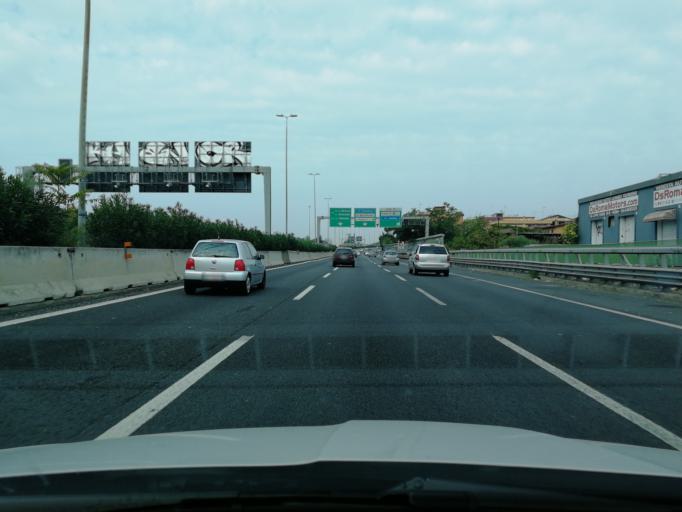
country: IT
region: Latium
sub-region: Citta metropolitana di Roma Capitale
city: Ciampino
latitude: 41.8598
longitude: 12.5995
